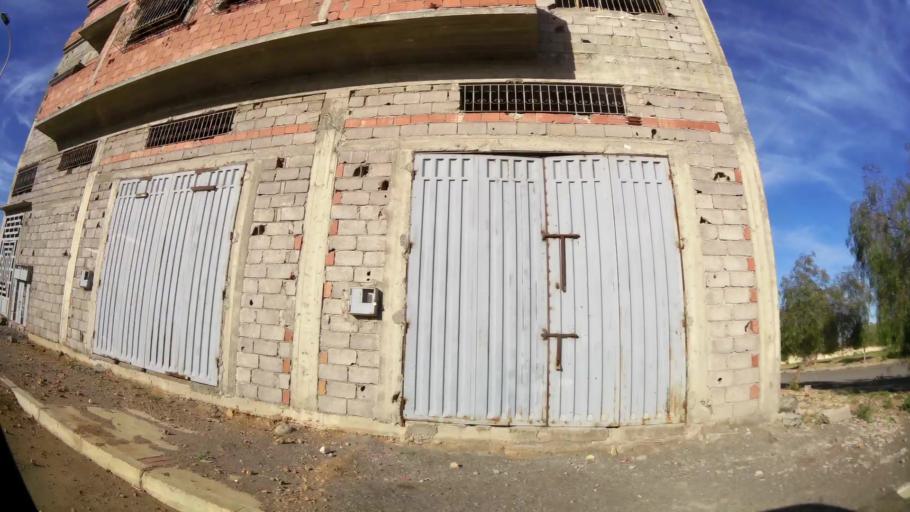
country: MA
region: Marrakech-Tensift-Al Haouz
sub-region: Marrakech
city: Marrakesh
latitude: 31.7590
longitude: -8.0936
